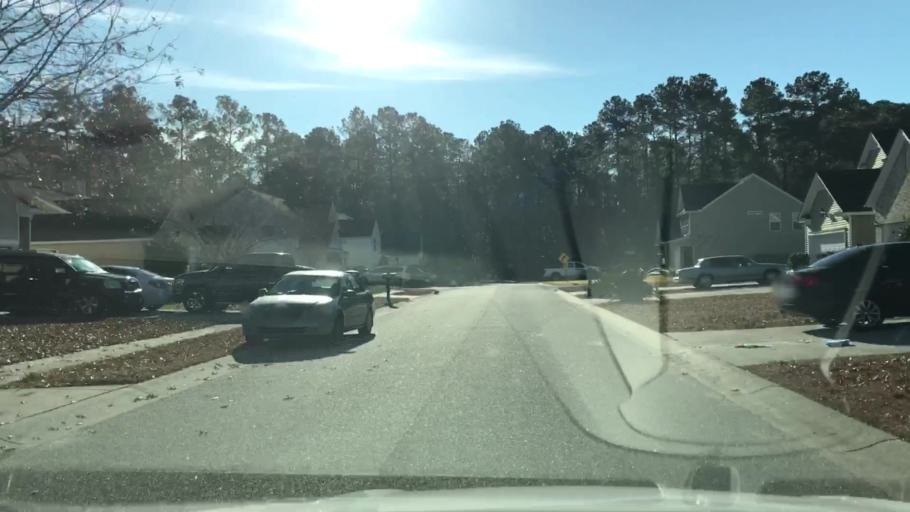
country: US
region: South Carolina
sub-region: Charleston County
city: Lincolnville
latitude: 32.9895
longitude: -80.1448
